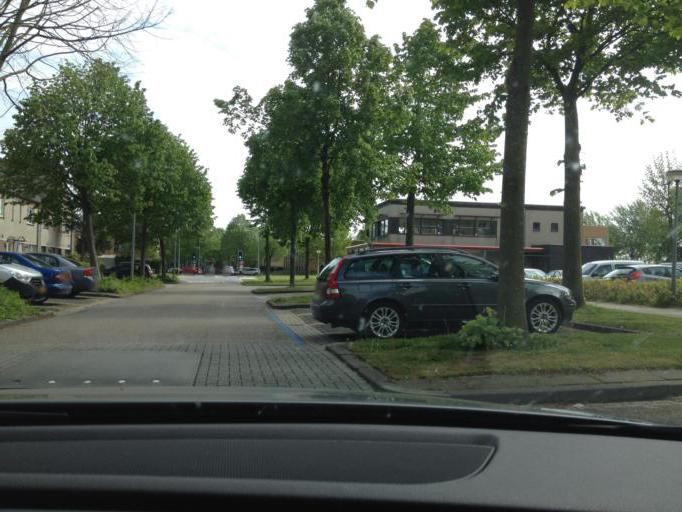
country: NL
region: Flevoland
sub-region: Gemeente Almere
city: Almere Stad
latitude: 52.3721
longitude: 5.2271
